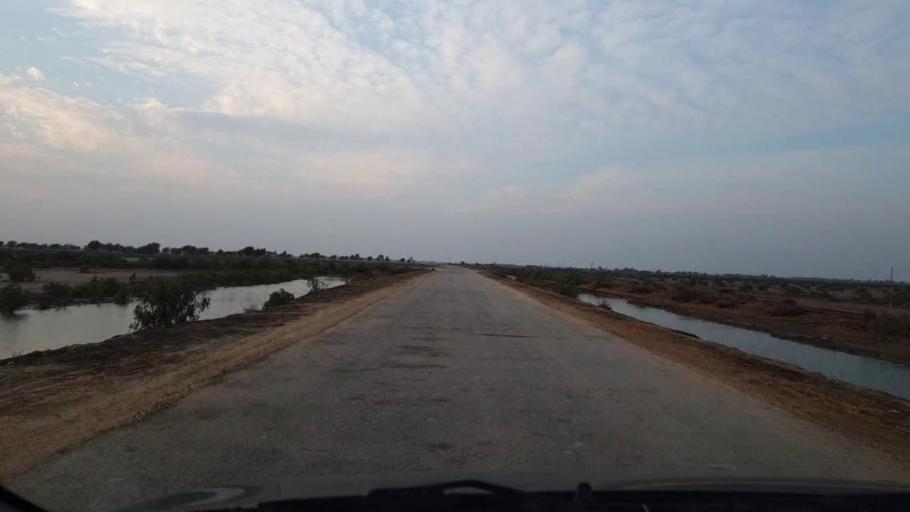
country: PK
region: Sindh
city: Sinjhoro
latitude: 26.0036
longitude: 68.8425
